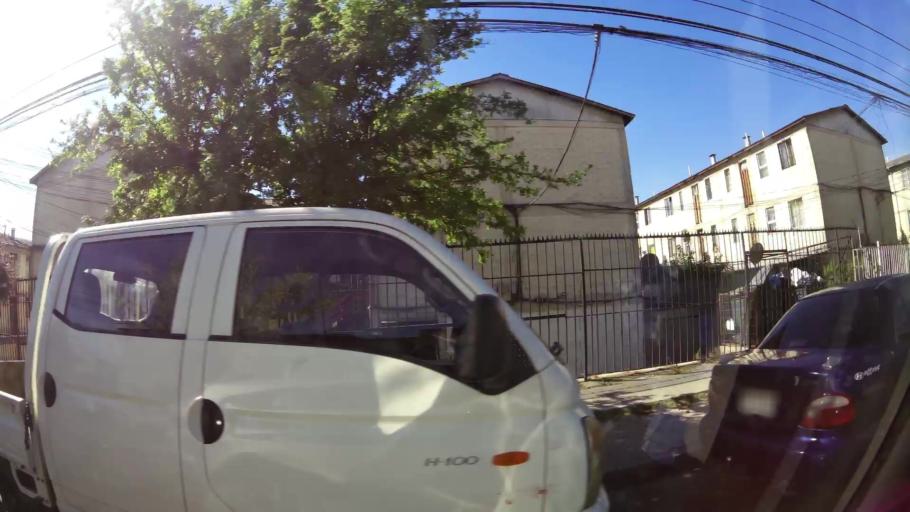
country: CL
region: Santiago Metropolitan
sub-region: Provincia de Santiago
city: Lo Prado
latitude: -33.4935
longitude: -70.7343
